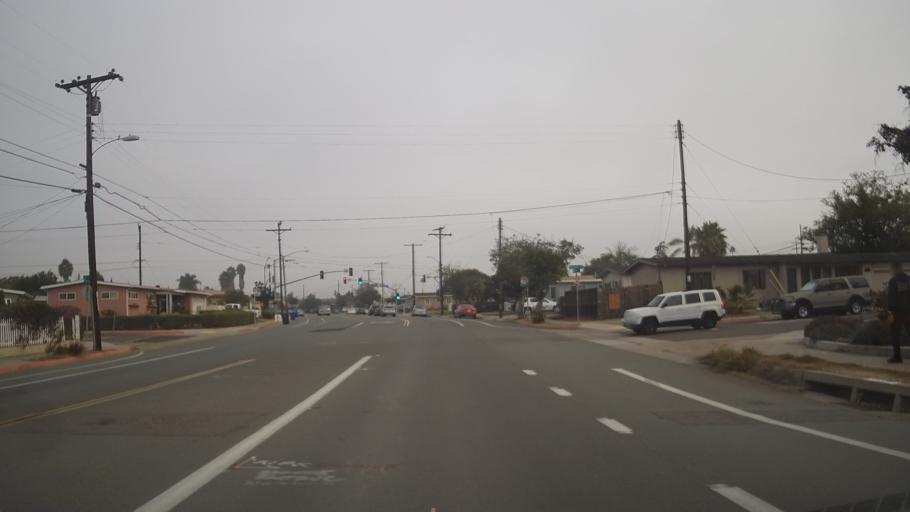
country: US
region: California
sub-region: San Diego County
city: San Diego
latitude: 32.7970
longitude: -117.1431
